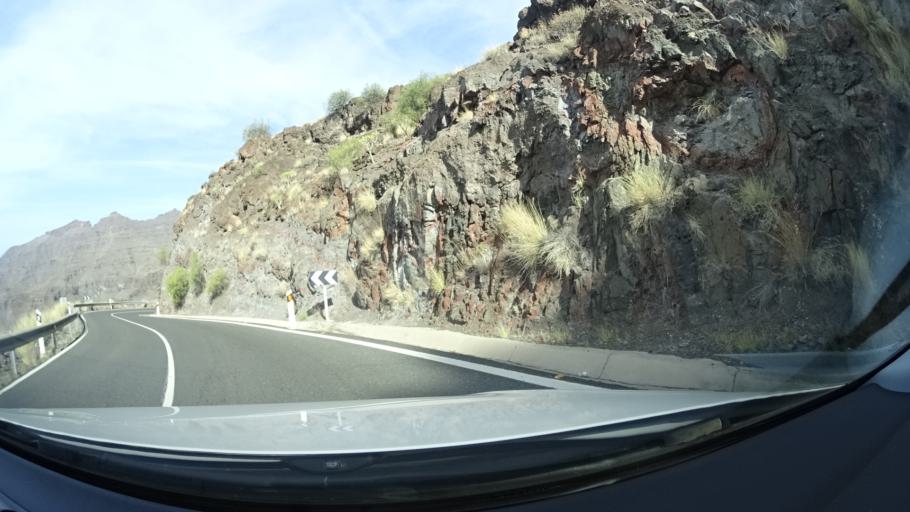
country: ES
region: Canary Islands
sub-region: Provincia de Las Palmas
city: Mogan
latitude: 27.8972
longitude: -15.7220
